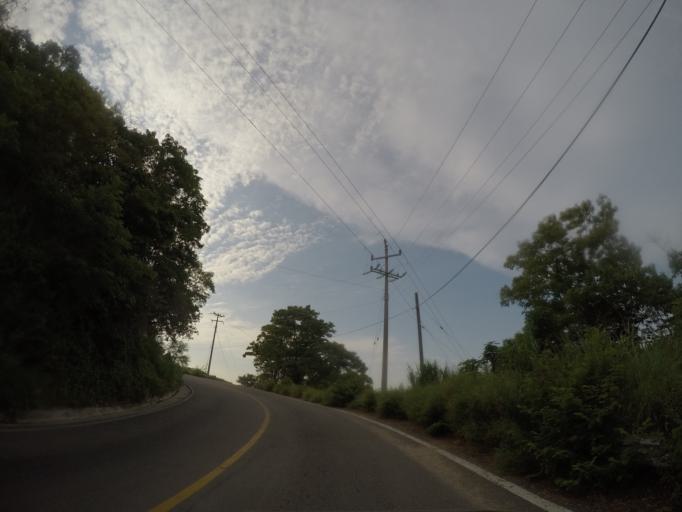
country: MX
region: Oaxaca
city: San Pedro Pochutla
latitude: 15.7034
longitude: -96.4813
